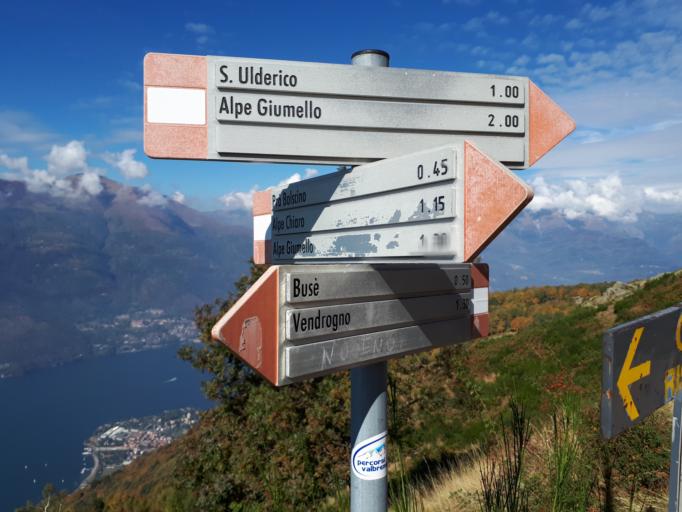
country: IT
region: Lombardy
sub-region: Provincia di Lecco
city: Introzzo
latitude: 46.0597
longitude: 9.3329
